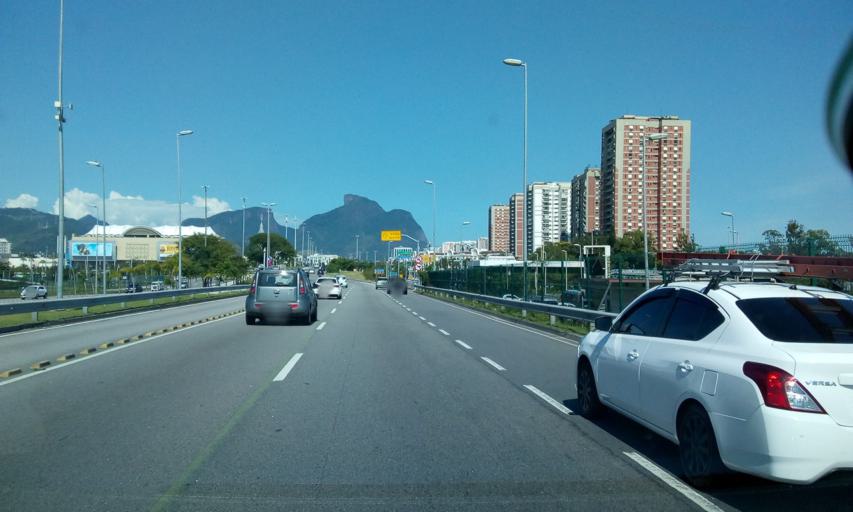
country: BR
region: Rio de Janeiro
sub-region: Rio De Janeiro
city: Rio de Janeiro
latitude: -23.0004
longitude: -43.3663
